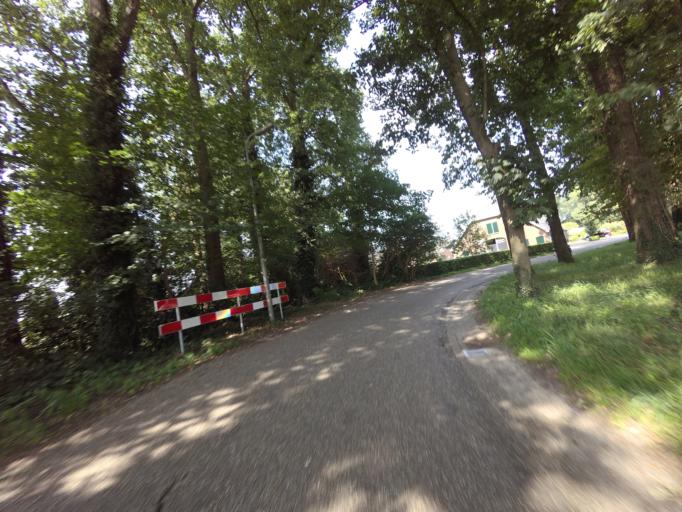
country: NL
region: Overijssel
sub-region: Gemeente Borne
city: Borne
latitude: 52.3141
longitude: 6.7142
